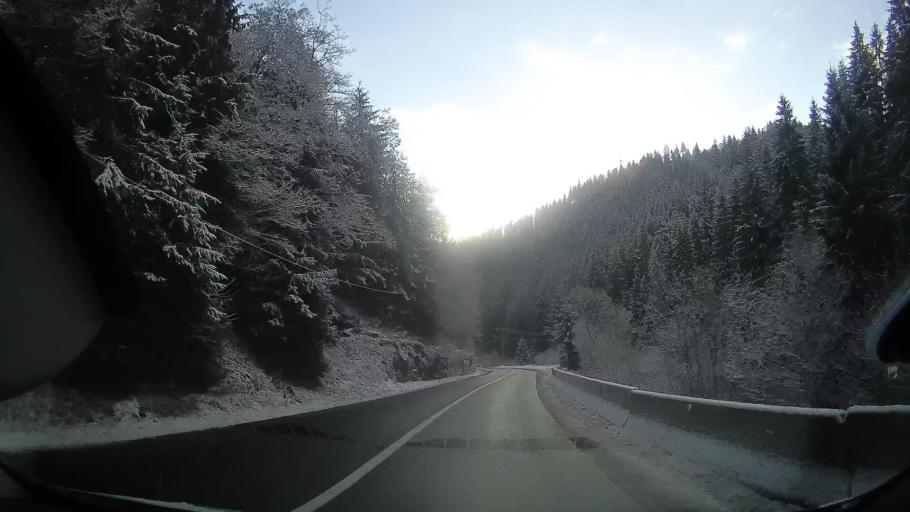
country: RO
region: Alba
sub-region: Comuna Scarisoara
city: Scarisoara
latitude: 46.4552
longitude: 22.8561
